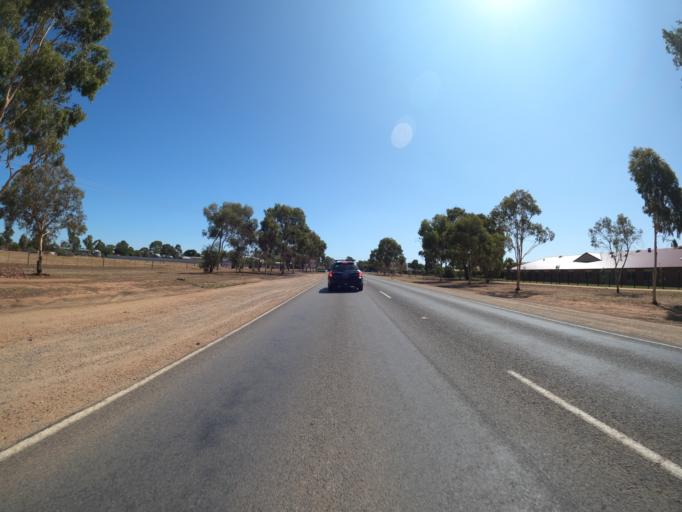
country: AU
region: Victoria
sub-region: Moira
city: Yarrawonga
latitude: -36.0144
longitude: 146.0154
